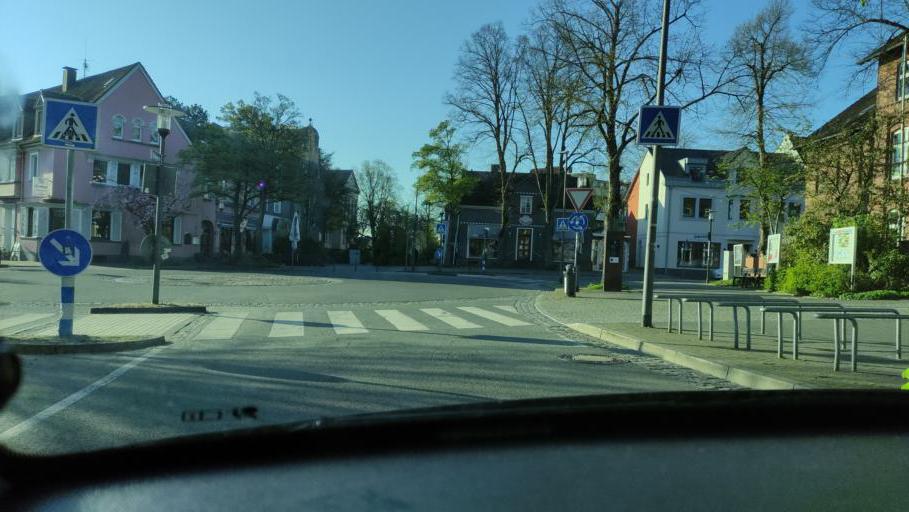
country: DE
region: North Rhine-Westphalia
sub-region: Regierungsbezirk Dusseldorf
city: Velbert
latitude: 51.4026
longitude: 7.0669
